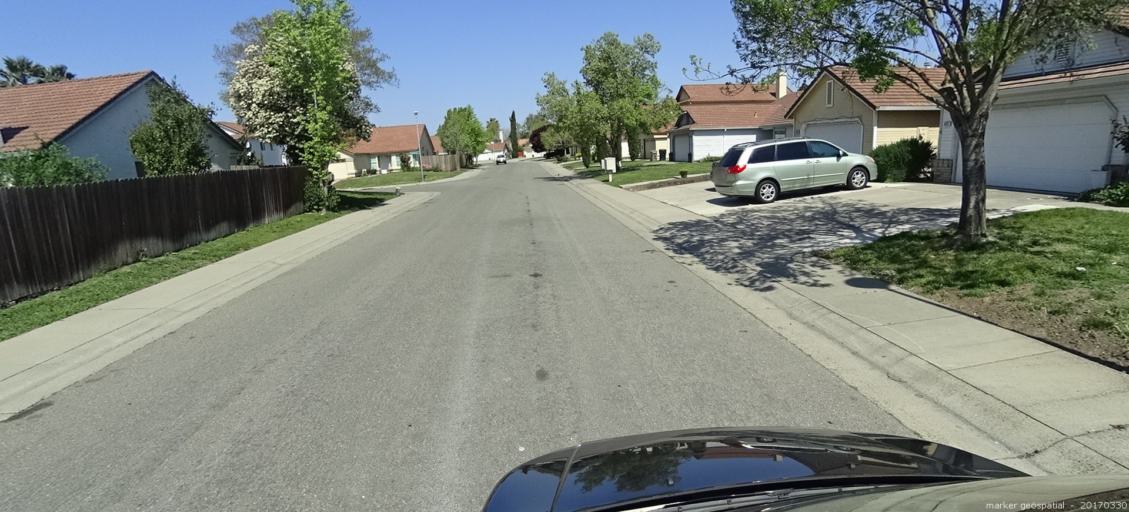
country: US
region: California
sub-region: Sacramento County
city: Florin
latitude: 38.4610
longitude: -121.4187
